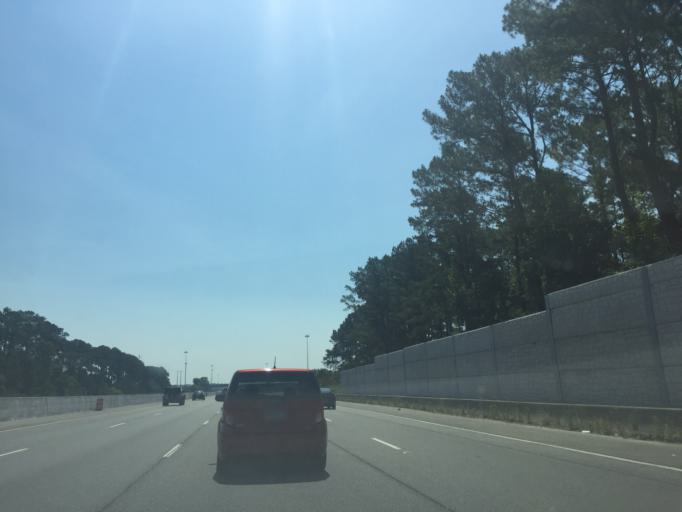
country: US
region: Georgia
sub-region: Chatham County
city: Georgetown
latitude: 31.9846
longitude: -81.2080
